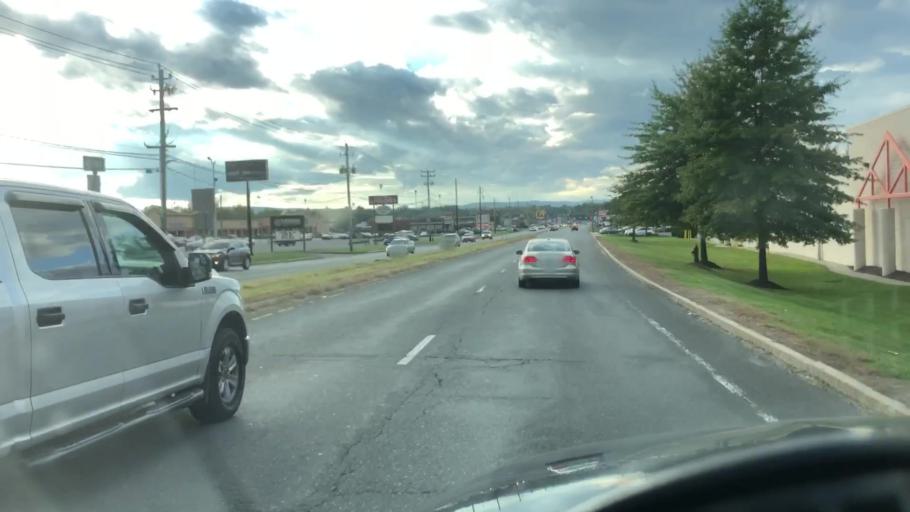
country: US
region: Massachusetts
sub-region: Hampden County
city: Westfield
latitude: 42.1128
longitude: -72.7205
